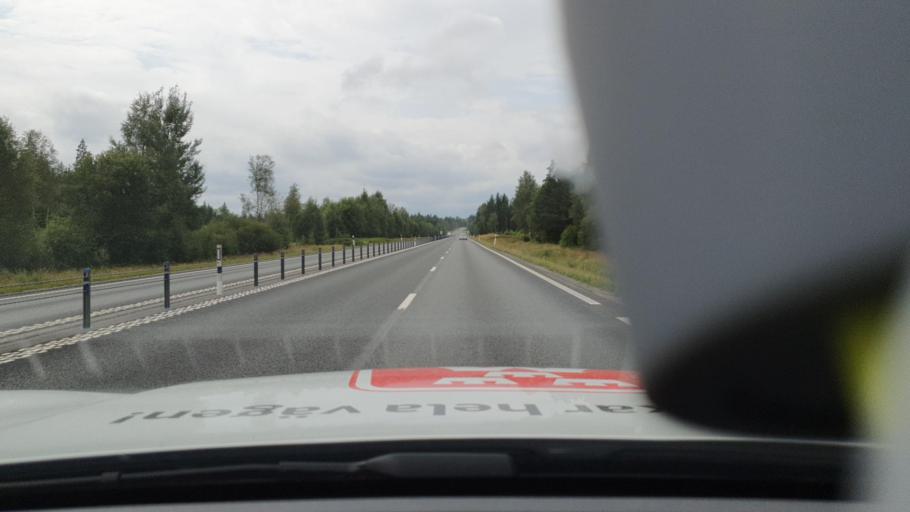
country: SE
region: Joenkoeping
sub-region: Gislaveds Kommun
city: Gislaved
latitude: 57.2769
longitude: 13.5041
